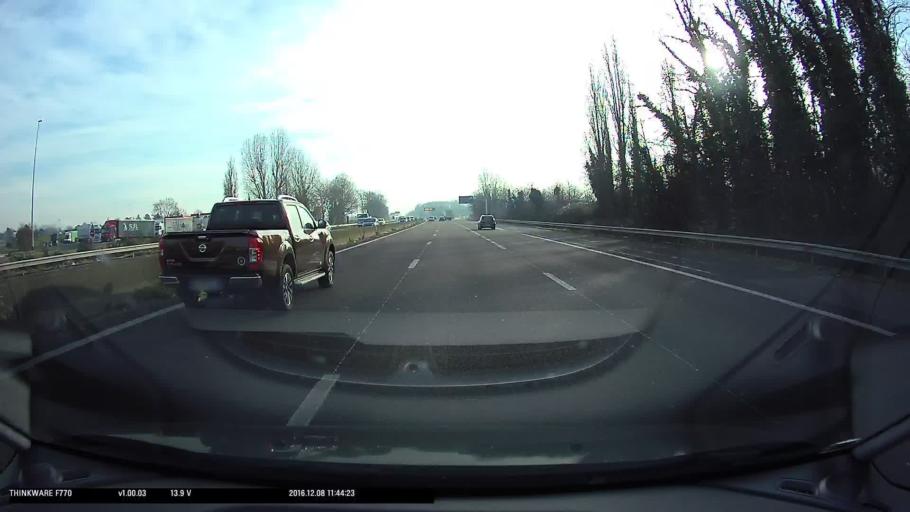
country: FR
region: Ile-de-France
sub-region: Departement du Val-d'Oise
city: Pierrelaye
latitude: 49.0162
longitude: 2.1439
